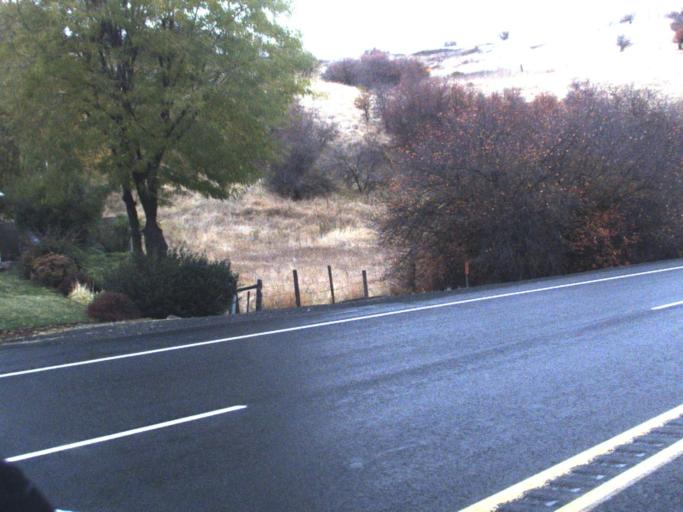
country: US
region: Washington
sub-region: Whitman County
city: Colfax
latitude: 46.8567
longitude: -117.3487
